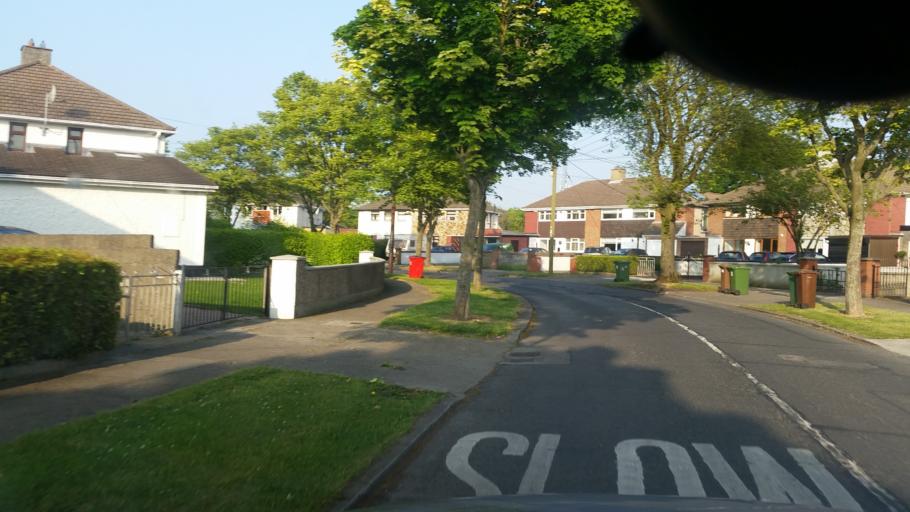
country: IE
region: Leinster
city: Glasnevin
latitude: 53.3904
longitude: -6.2551
